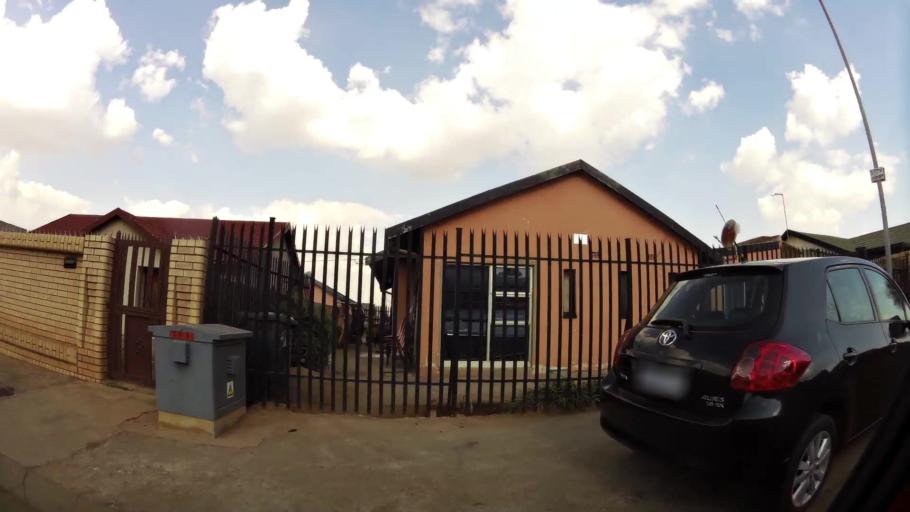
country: ZA
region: Gauteng
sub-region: City of Johannesburg Metropolitan Municipality
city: Roodepoort
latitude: -26.2106
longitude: 27.8673
